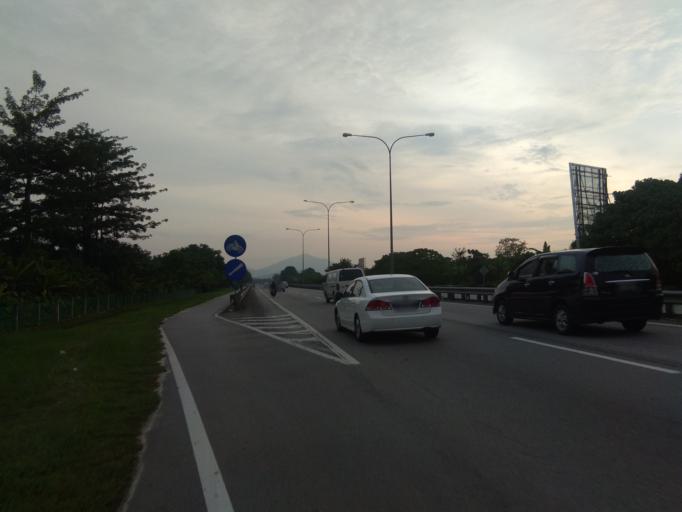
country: MY
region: Kedah
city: Kulim
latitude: 5.4305
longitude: 100.5489
